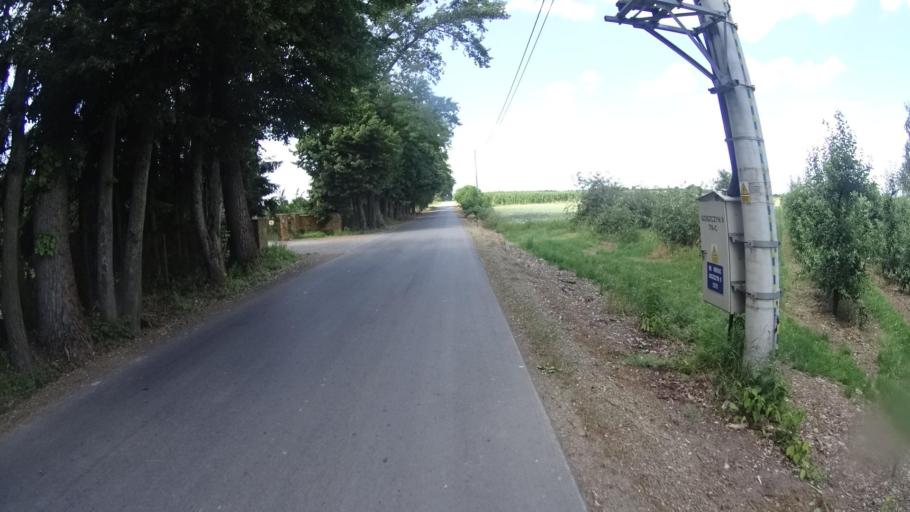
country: PL
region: Masovian Voivodeship
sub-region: Powiat grojecki
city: Goszczyn
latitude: 51.7245
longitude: 20.8673
